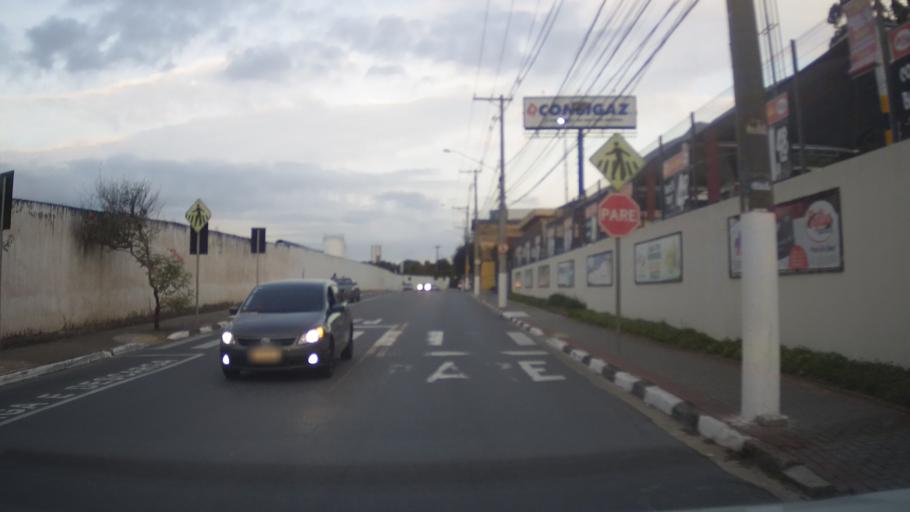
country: BR
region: Sao Paulo
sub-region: Aruja
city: Aruja
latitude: -23.3965
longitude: -46.3292
